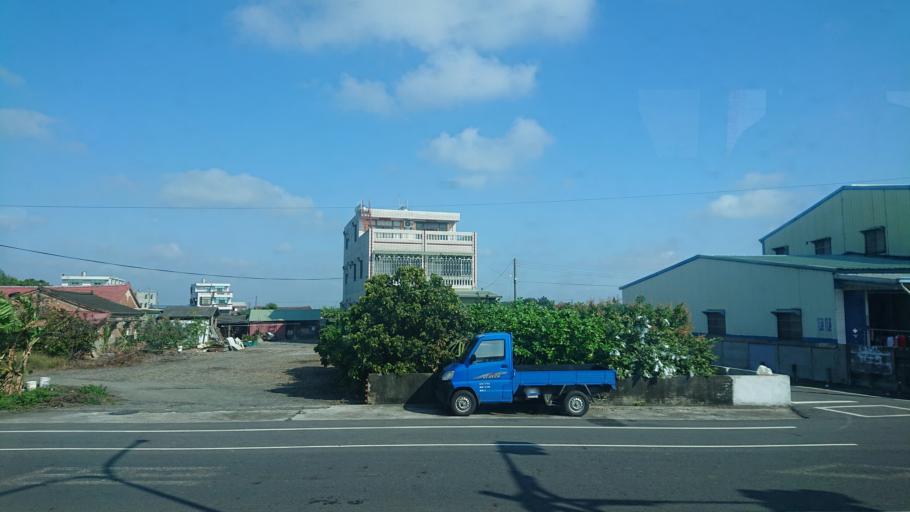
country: TW
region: Taiwan
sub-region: Chiayi
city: Taibao
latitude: 23.4569
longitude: 120.3139
